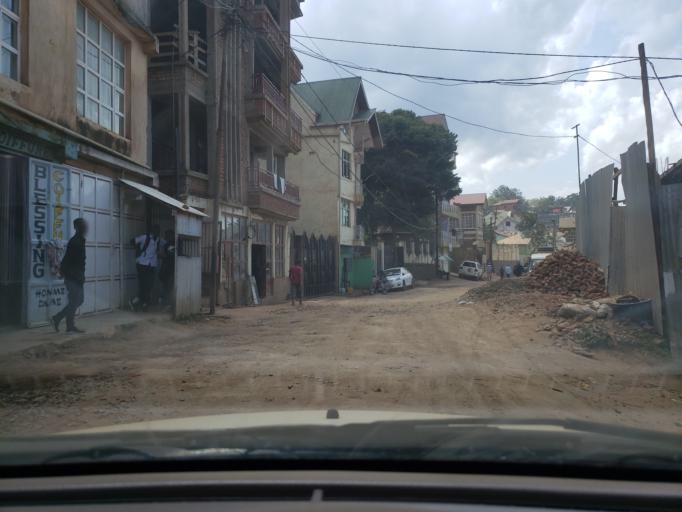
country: CD
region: South Kivu
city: Bukavu
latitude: -2.5015
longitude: 28.8725
